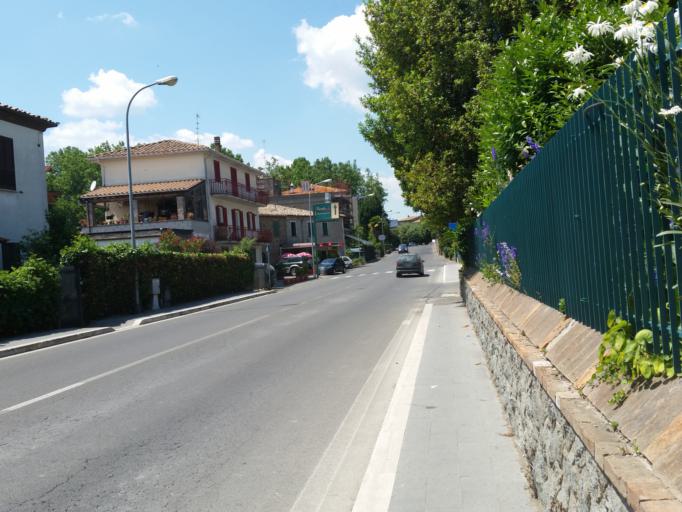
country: IT
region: Latium
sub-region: Provincia di Viterbo
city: Bolsena
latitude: 42.6428
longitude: 11.9880
